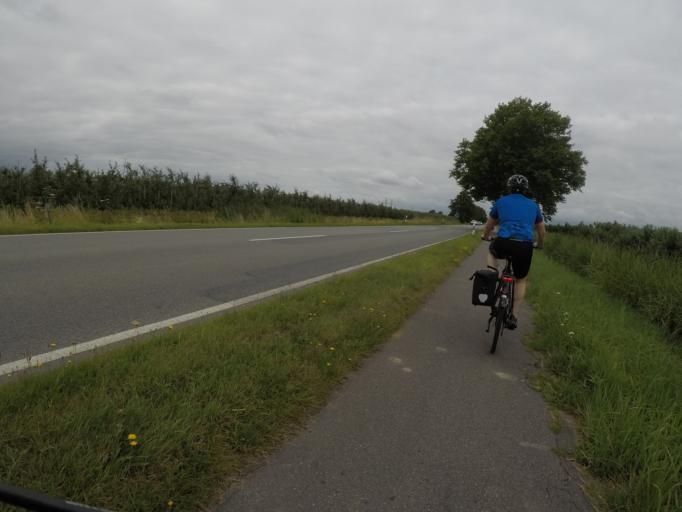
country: DE
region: Lower Saxony
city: Mittelnkirchen
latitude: 53.5395
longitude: 9.6449
